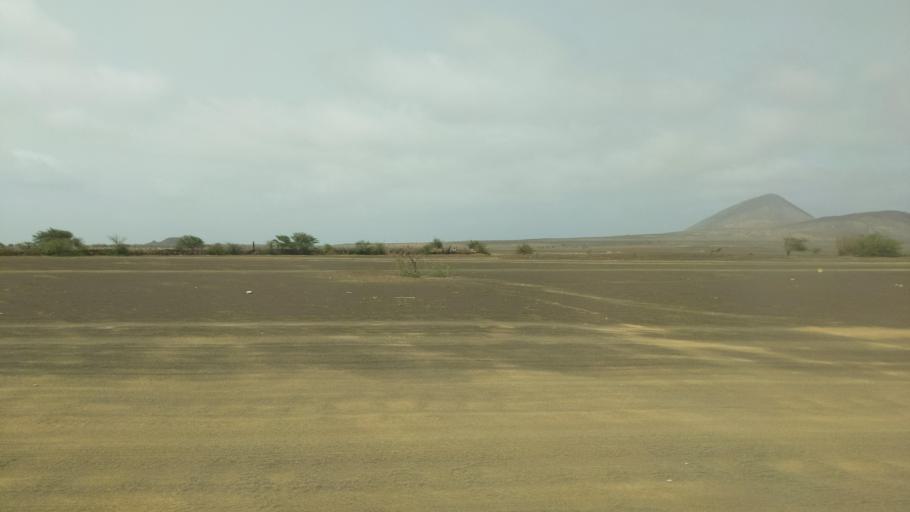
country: CV
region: Sal
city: Espargos
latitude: 16.7959
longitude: -22.9535
